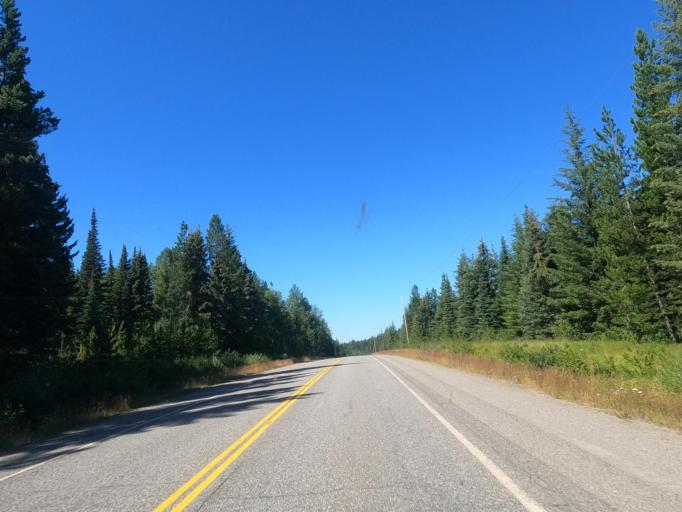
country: CA
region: British Columbia
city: Quesnel
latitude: 53.0274
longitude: -122.0425
